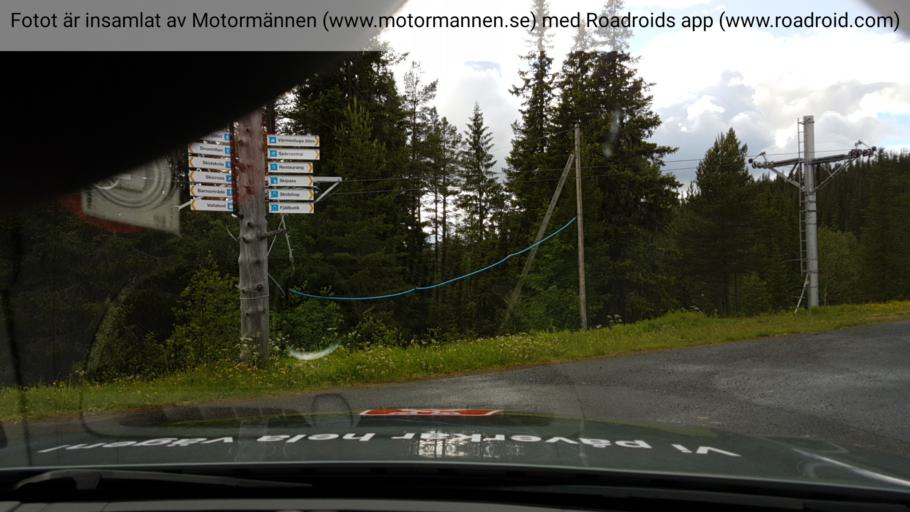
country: SE
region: Jaemtland
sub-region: Are Kommun
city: Jarpen
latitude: 63.0849
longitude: 13.7737
